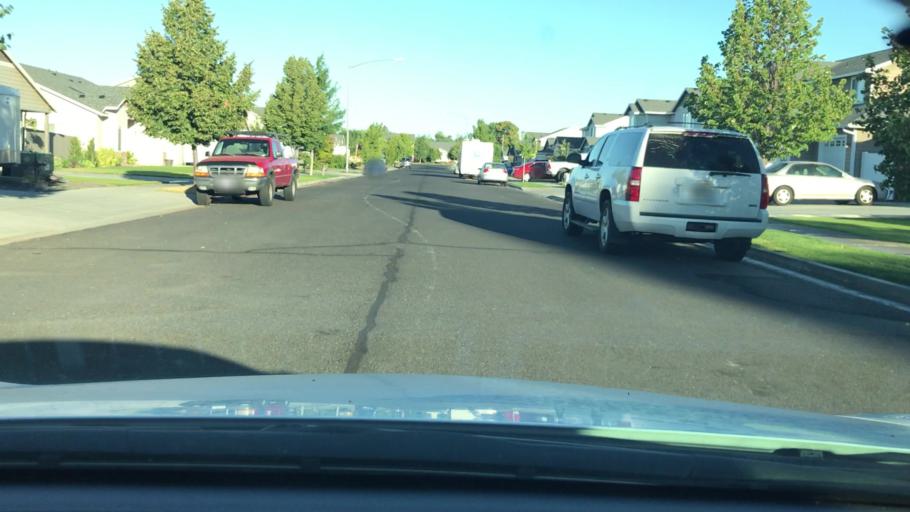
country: US
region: Washington
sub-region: Grant County
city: Moses Lake
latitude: 47.1207
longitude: -119.2529
